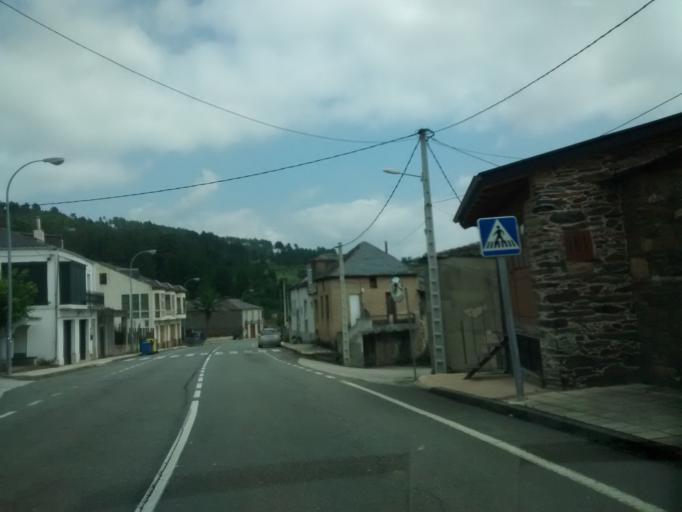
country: ES
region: Galicia
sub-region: Provincia de Ourense
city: Petin
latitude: 42.3454
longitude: -7.1703
